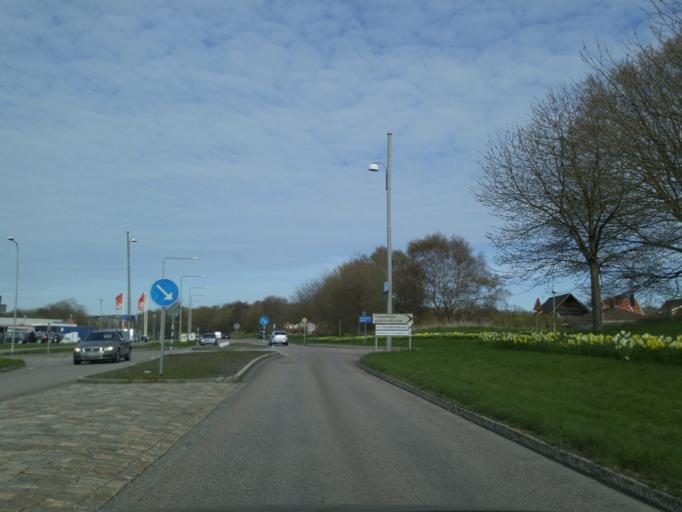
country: SE
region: Vaestra Goetaland
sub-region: Goteborg
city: Majorna
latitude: 57.6550
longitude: 11.8742
